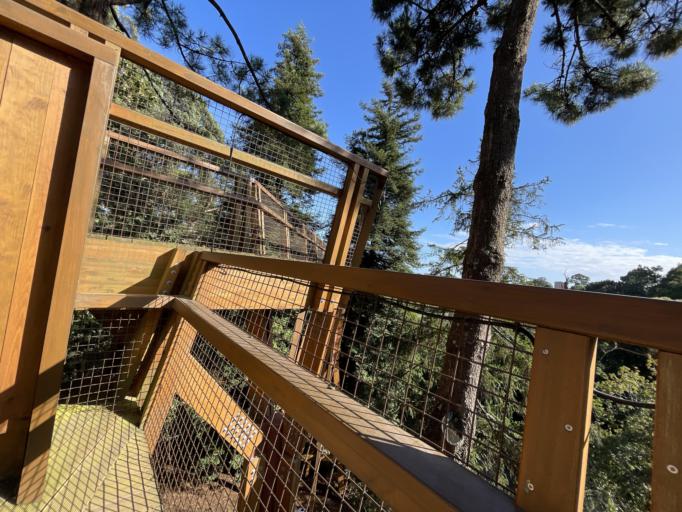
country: PT
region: Porto
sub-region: Matosinhos
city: Senhora da Hora
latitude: 41.1577
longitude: -8.6562
